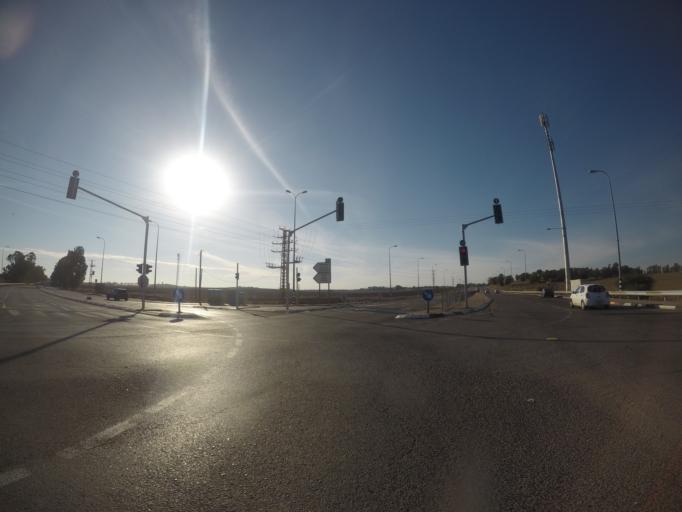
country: IL
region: Southern District
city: Qiryat Gat
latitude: 31.6459
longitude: 34.6997
